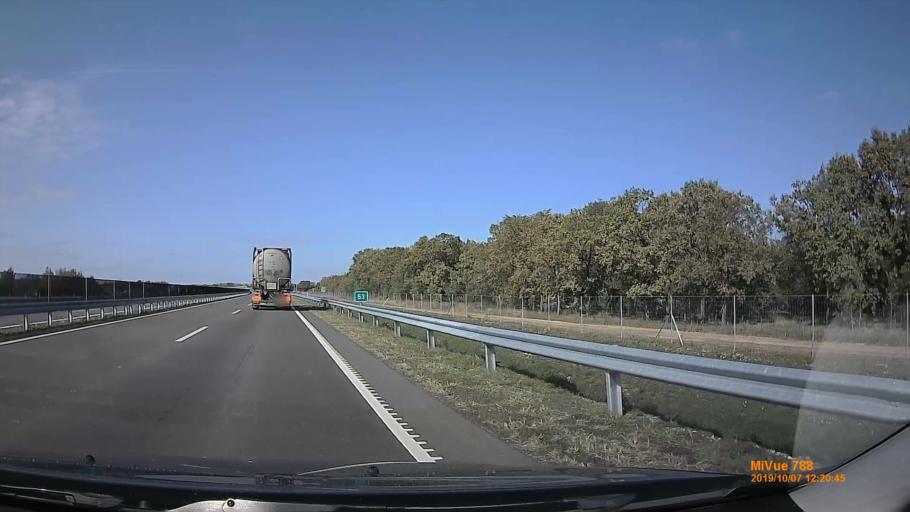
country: HU
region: Jasz-Nagykun-Szolnok
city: Kunszentmarton
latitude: 46.8572
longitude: 20.3092
